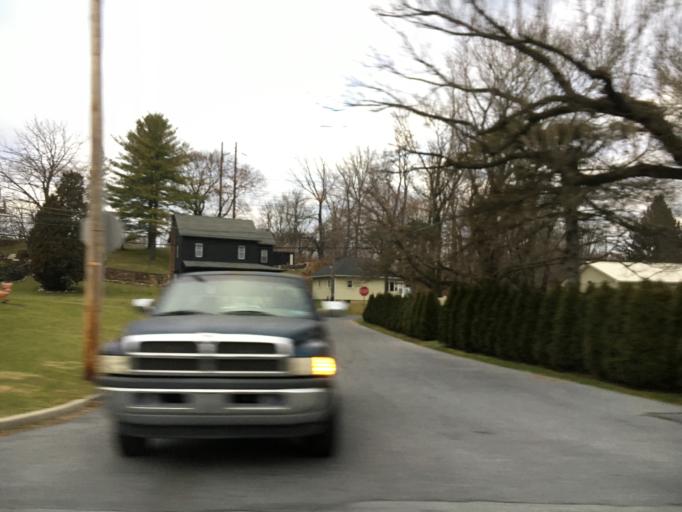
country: US
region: Pennsylvania
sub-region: Lehigh County
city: Egypt
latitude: 40.6795
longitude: -75.5379
